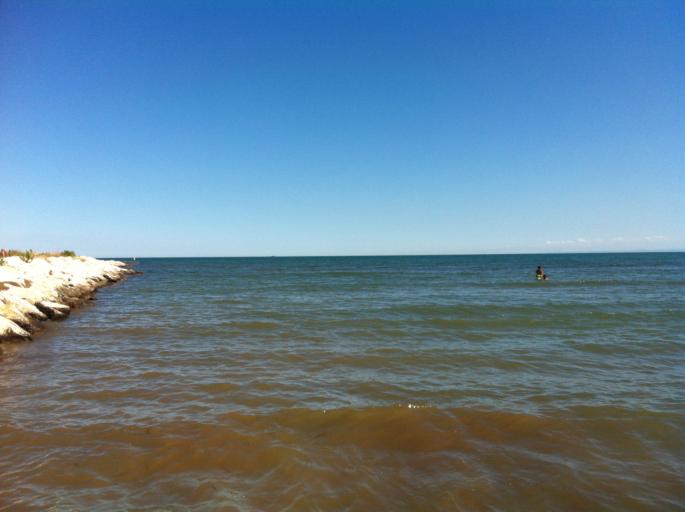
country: IT
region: Apulia
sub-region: Provincia di Foggia
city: Manfredonia
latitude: 41.6173
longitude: 15.9029
